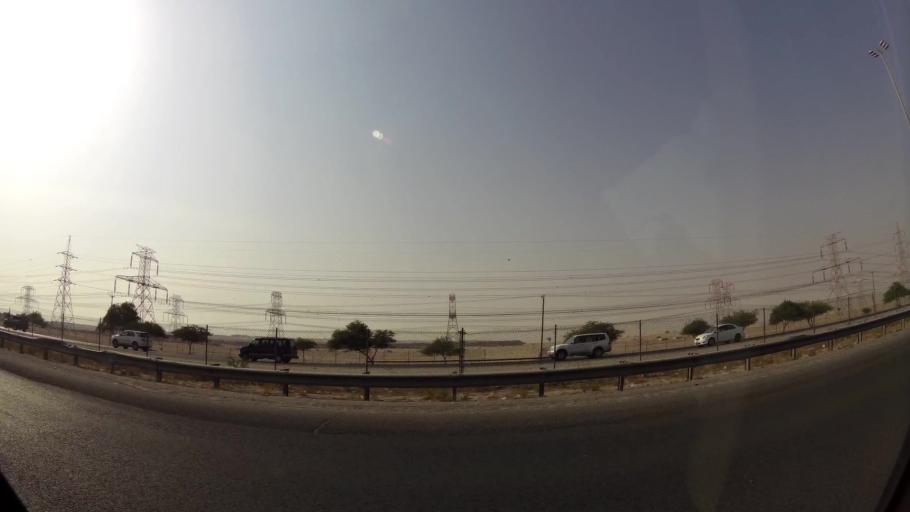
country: KW
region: Al Farwaniyah
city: Al Farwaniyah
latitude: 29.1831
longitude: 47.9100
